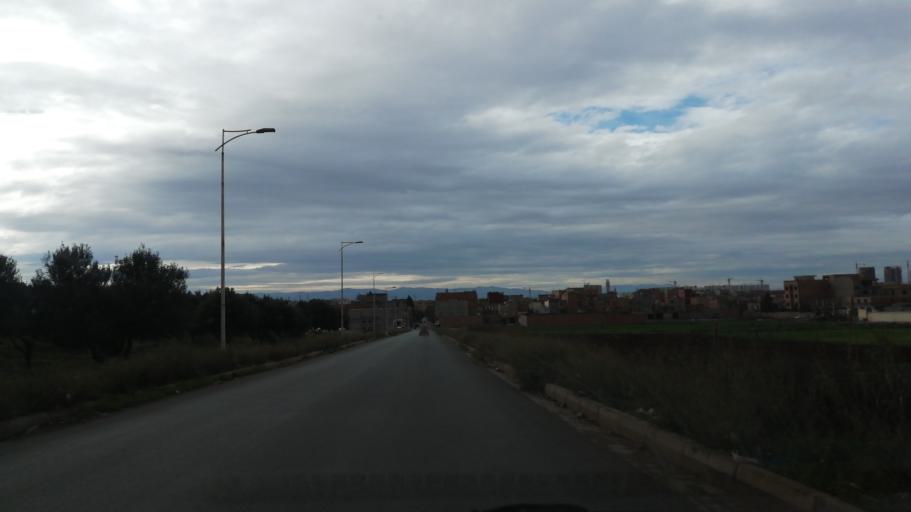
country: DZ
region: Oran
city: Oran
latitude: 35.6898
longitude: -0.5969
